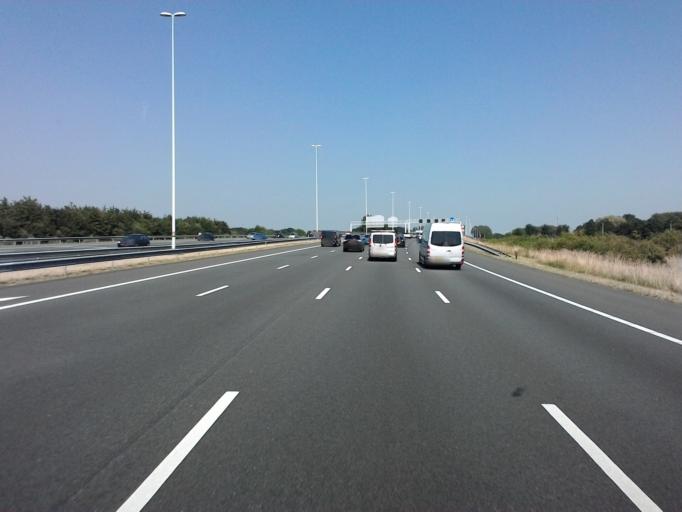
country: NL
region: Utrecht
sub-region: Gemeente Bunnik
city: Bunnik
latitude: 52.0614
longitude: 5.1675
